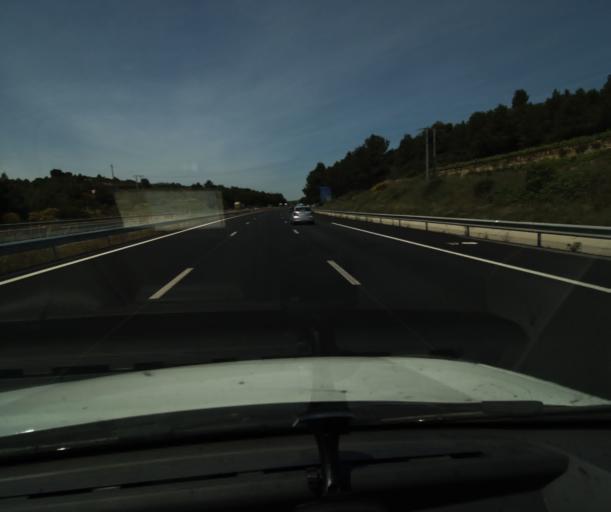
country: FR
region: Languedoc-Roussillon
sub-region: Departement de l'Aude
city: Sigean
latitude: 43.0075
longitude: 2.9566
